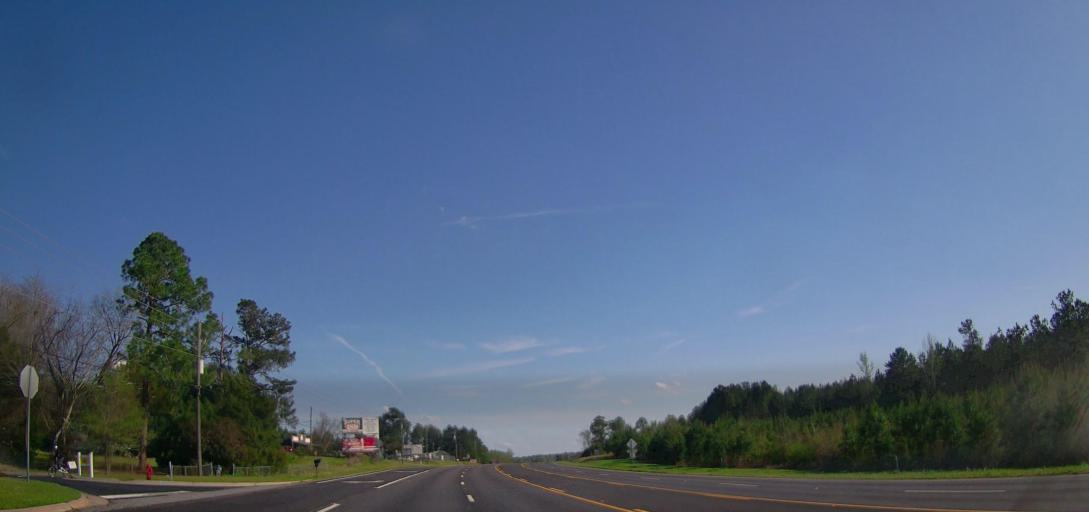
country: US
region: Georgia
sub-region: Baldwin County
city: Milledgeville
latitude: 33.1720
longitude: -83.2818
